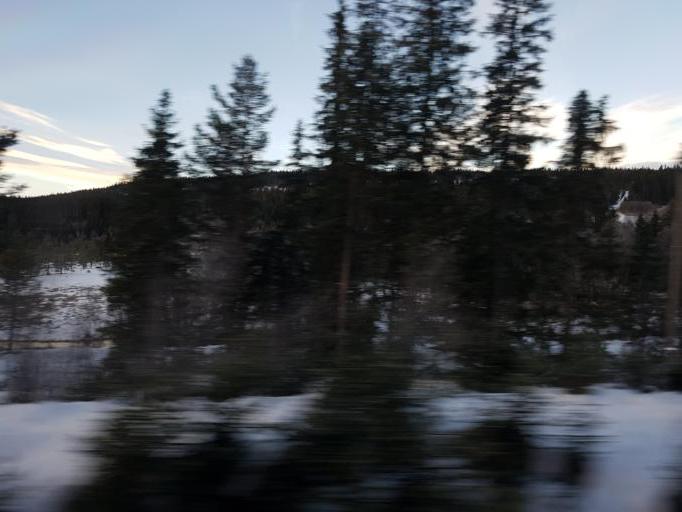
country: NO
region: Sor-Trondelag
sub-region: Rennebu
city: Berkak
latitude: 62.8513
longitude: 10.0237
